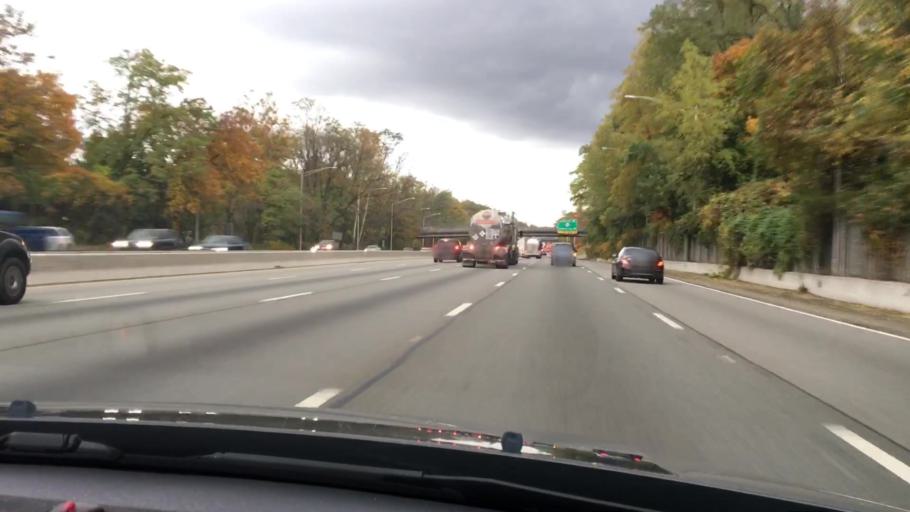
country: US
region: New Jersey
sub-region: Morris County
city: Morristown
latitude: 40.7933
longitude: -74.4688
